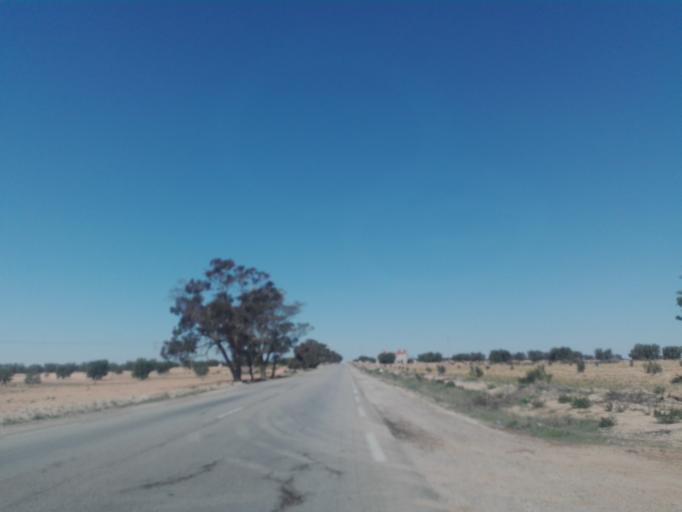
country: TN
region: Safaqis
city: Bi'r `Ali Bin Khalifah
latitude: 34.7524
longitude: 10.3412
